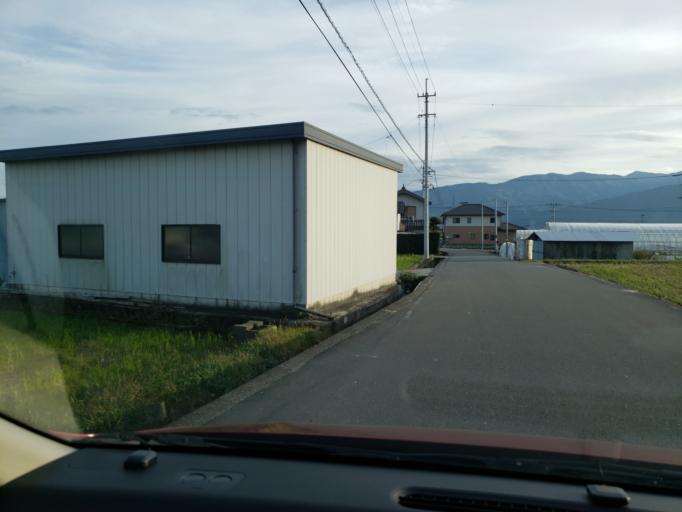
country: JP
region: Tokushima
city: Wakimachi
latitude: 34.0838
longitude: 134.2271
